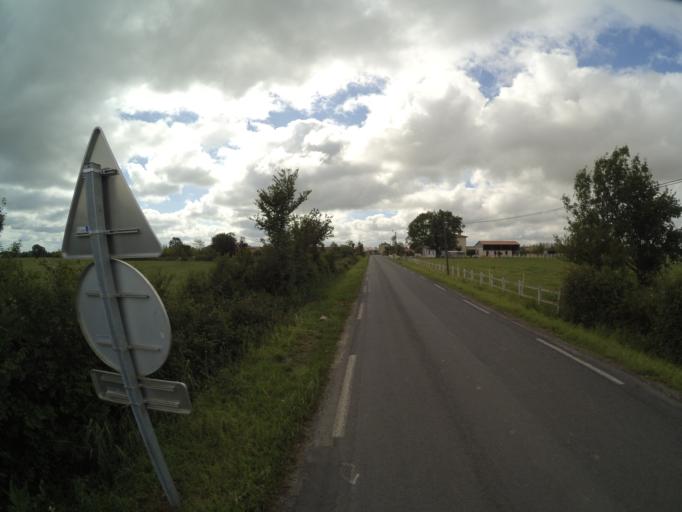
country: FR
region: Aquitaine
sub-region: Departement de la Gironde
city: Ludon-Medoc
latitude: 44.9931
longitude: -0.5870
